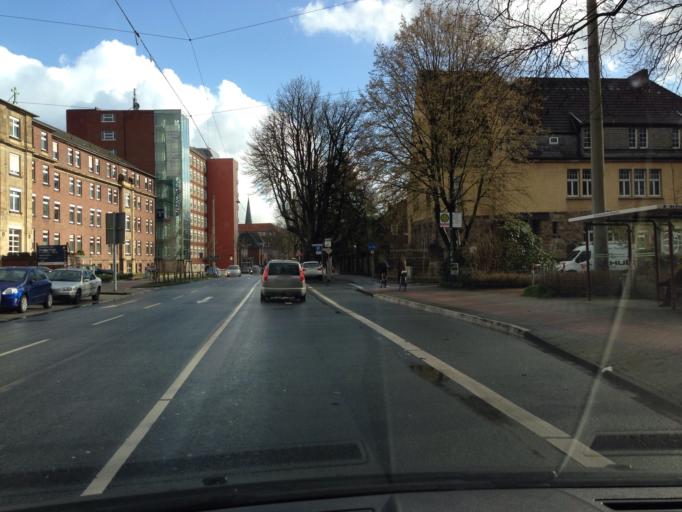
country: DE
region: North Rhine-Westphalia
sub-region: Regierungsbezirk Munster
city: Muenster
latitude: 51.9624
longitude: 7.6475
